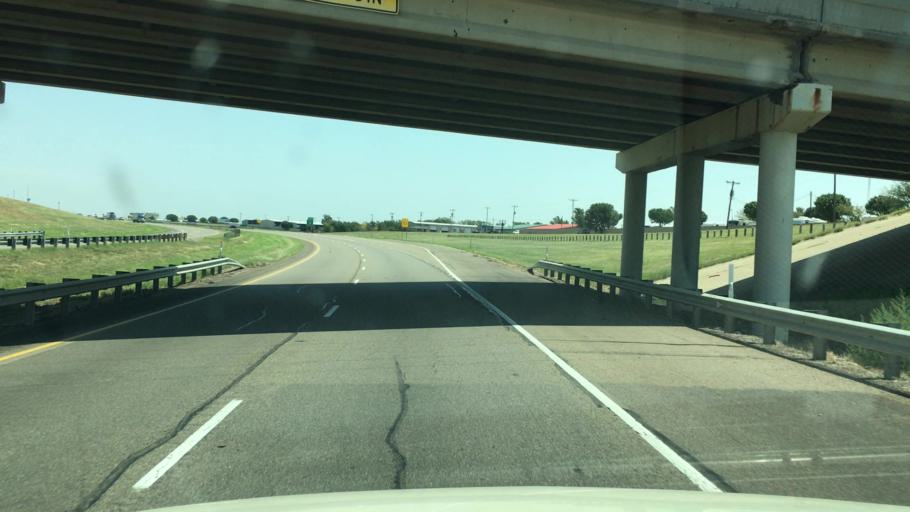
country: US
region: Texas
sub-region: Potter County
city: Bushland
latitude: 35.1873
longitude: -101.9745
